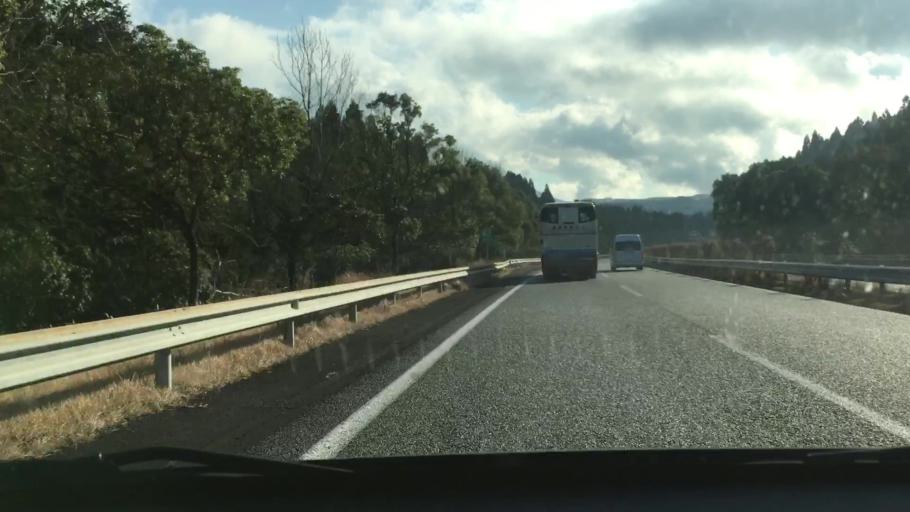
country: JP
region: Kagoshima
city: Okuchi-shinohara
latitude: 32.0320
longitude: 130.7981
